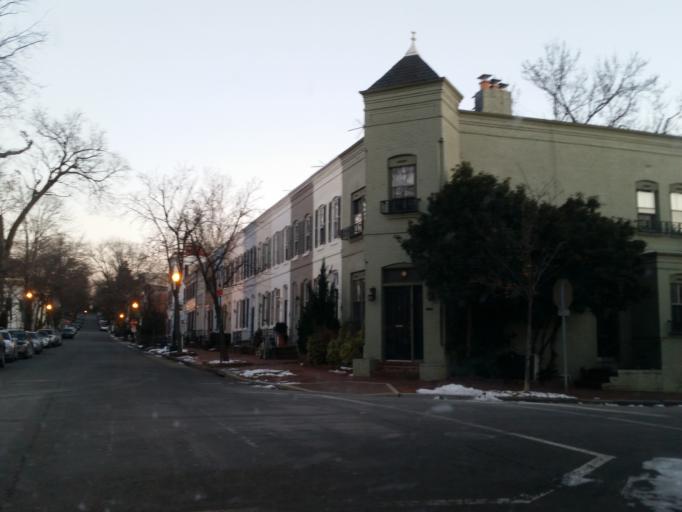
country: US
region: Washington, D.C.
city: Washington, D.C.
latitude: 38.9076
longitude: -77.0570
